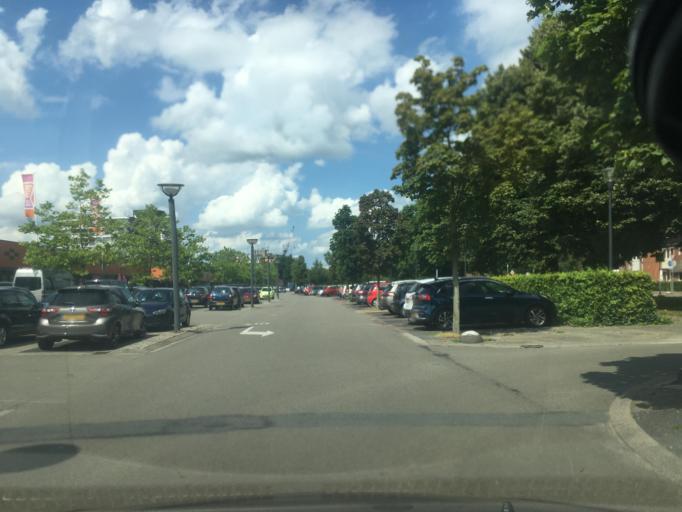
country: NL
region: Groningen
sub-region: Gemeente Hoogezand-Sappemeer
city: Hoogezand
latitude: 53.1543
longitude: 6.7589
